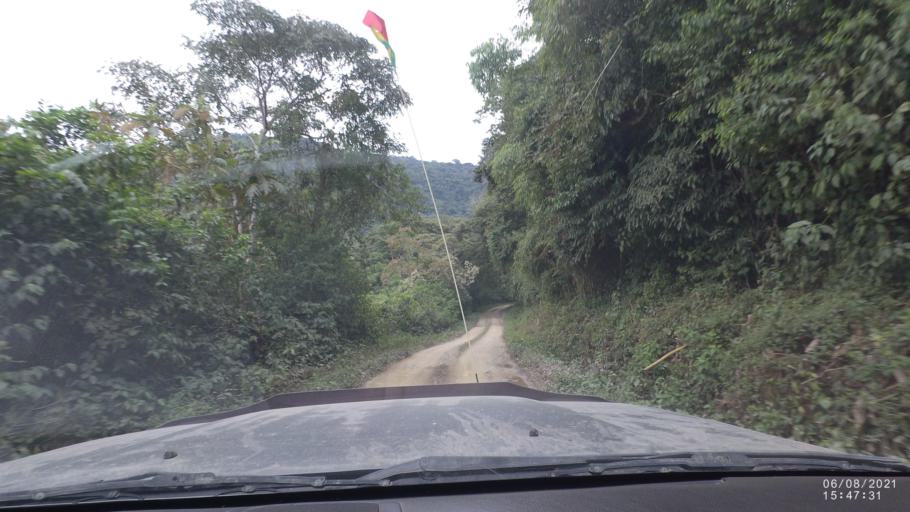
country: BO
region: La Paz
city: Quime
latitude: -16.5926
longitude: -66.7057
